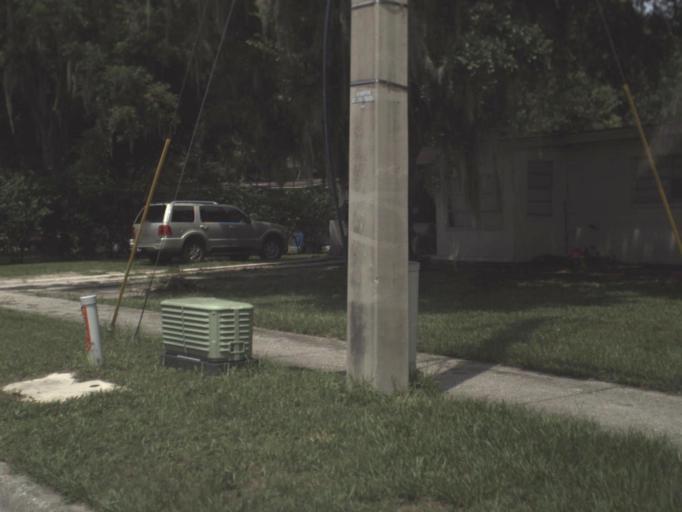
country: US
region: Florida
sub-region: Hillsborough County
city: Plant City
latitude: 27.9992
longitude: -82.1214
